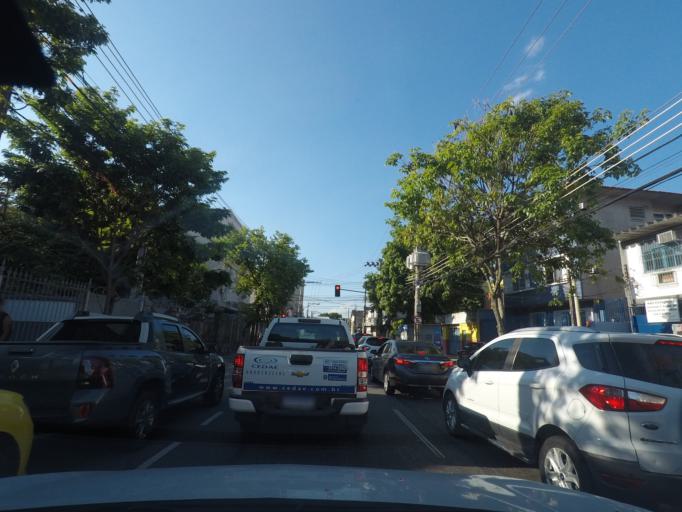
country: BR
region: Rio de Janeiro
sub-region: Rio De Janeiro
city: Rio de Janeiro
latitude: -22.8946
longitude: -43.2273
